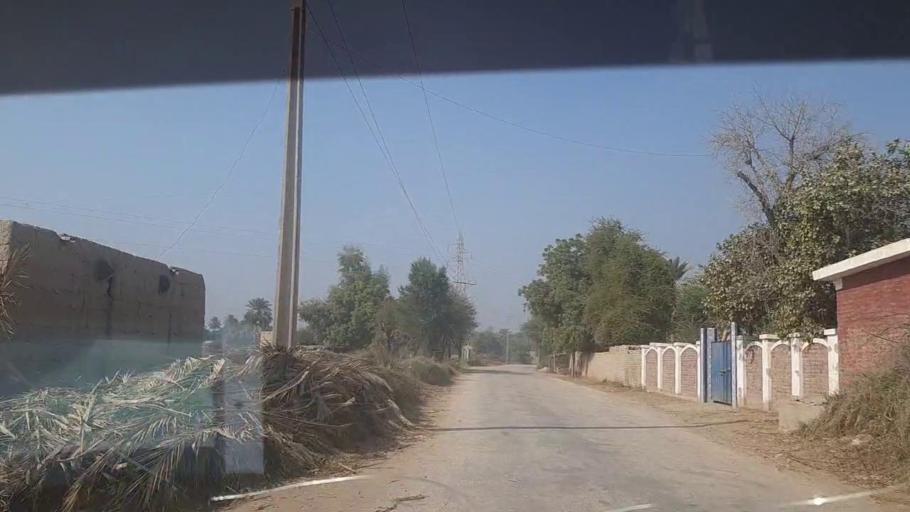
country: PK
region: Sindh
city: Kot Diji
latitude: 27.3645
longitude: 68.7043
